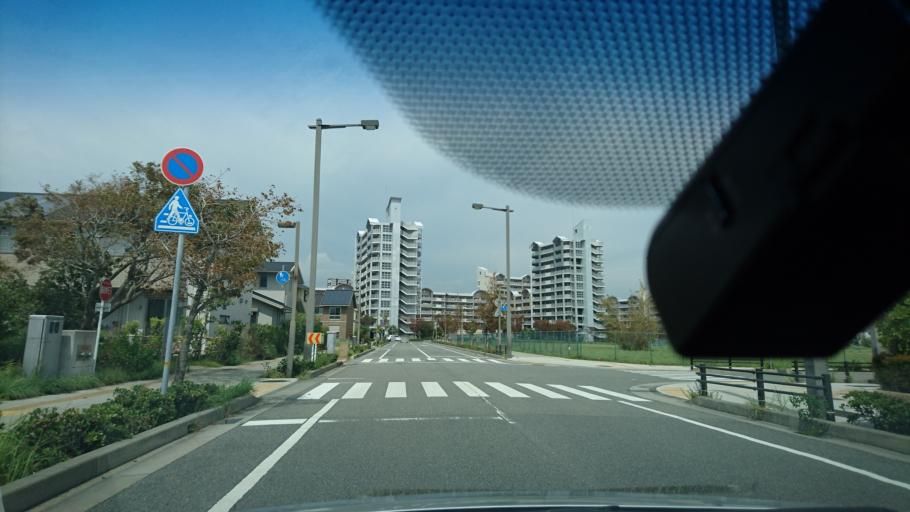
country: JP
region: Hyogo
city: Nishinomiya-hama
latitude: 34.7111
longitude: 135.3151
